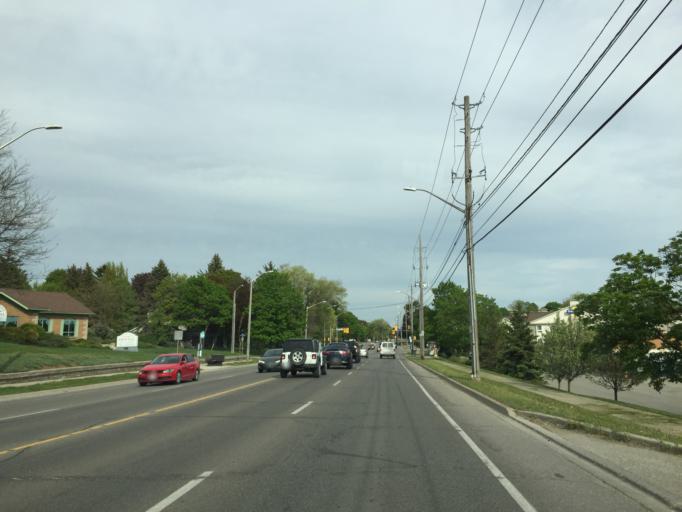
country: CA
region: Ontario
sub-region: Wellington County
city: Guelph
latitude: 43.5258
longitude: -80.2223
